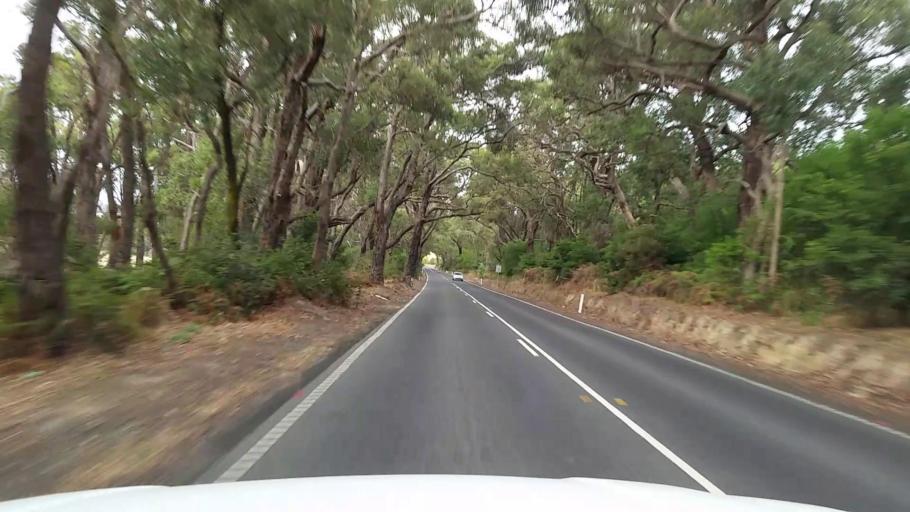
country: AU
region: Victoria
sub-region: Mornington Peninsula
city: Balnarring
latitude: -38.3346
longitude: 145.0957
